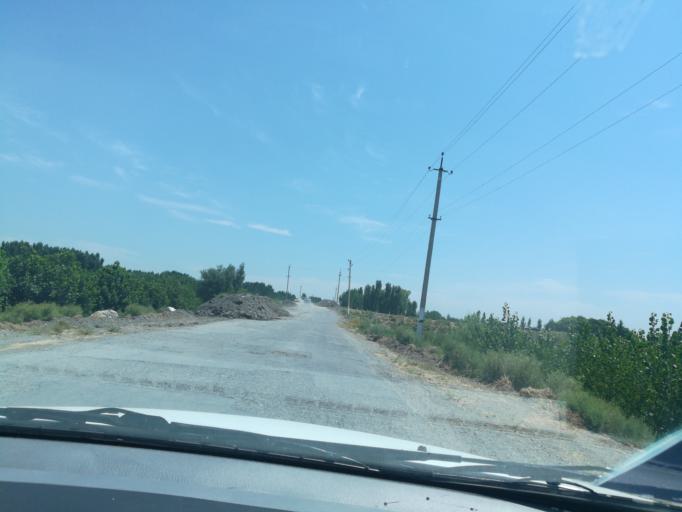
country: UZ
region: Namangan
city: Haqqulobod
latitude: 40.8997
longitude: 72.0016
